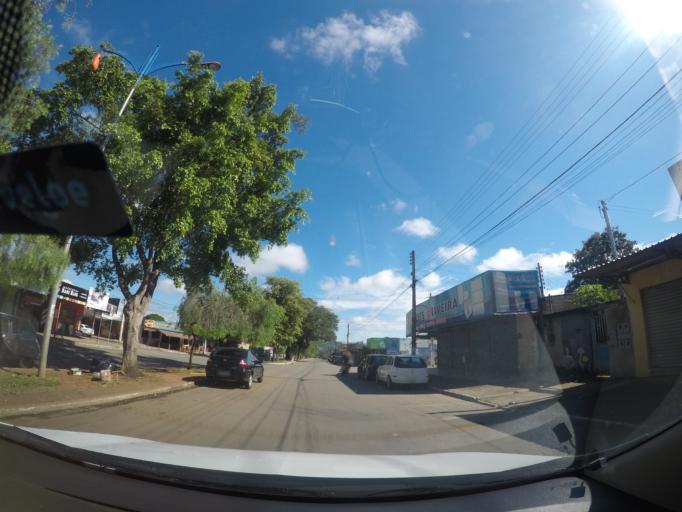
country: BR
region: Goias
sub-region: Senador Canedo
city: Senador Canedo
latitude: -16.6523
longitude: -49.1565
